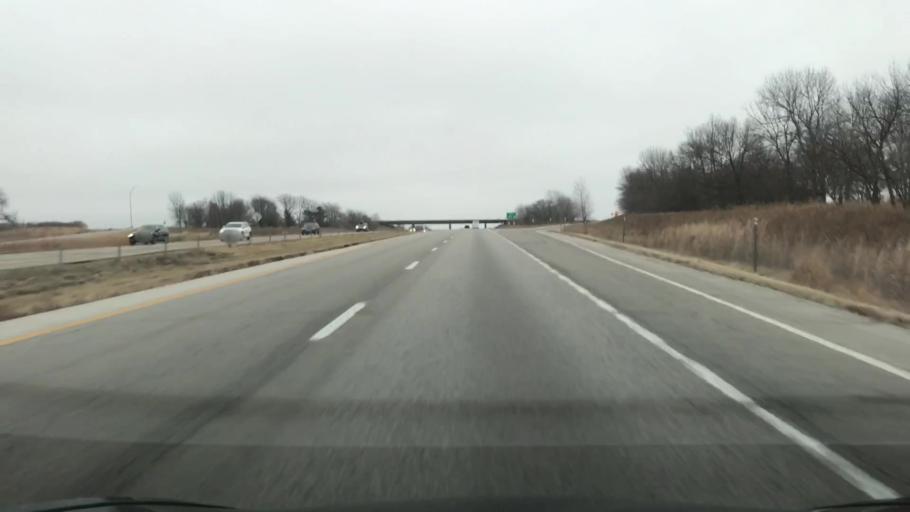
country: US
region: Iowa
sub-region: Madison County
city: Earlham
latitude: 41.5188
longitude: -94.0826
